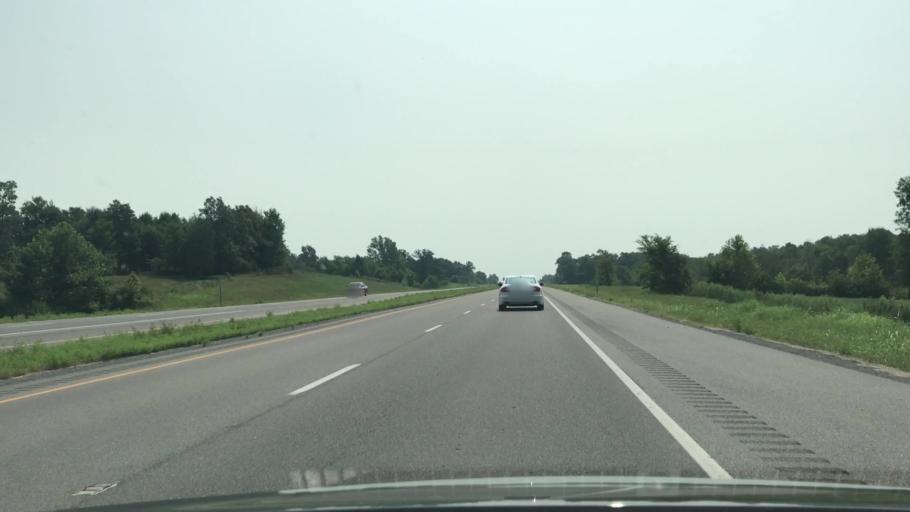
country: US
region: Kentucky
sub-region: Graves County
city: Mayfield
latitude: 36.6675
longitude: -88.4926
